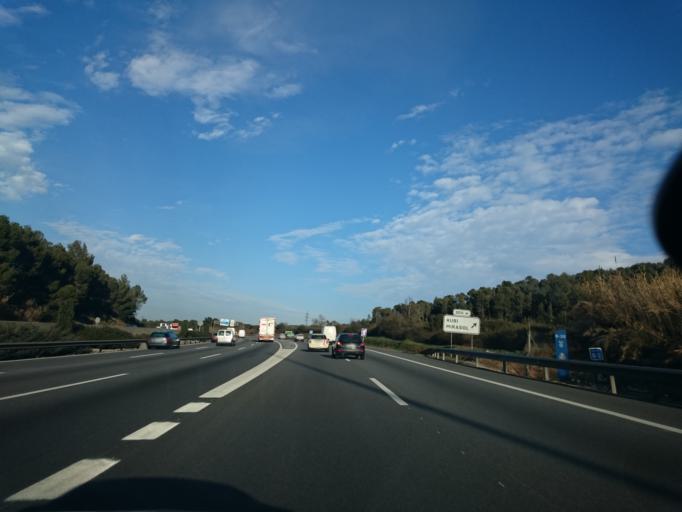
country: ES
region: Catalonia
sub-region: Provincia de Barcelona
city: Rubi
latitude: 41.4613
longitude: 2.0262
